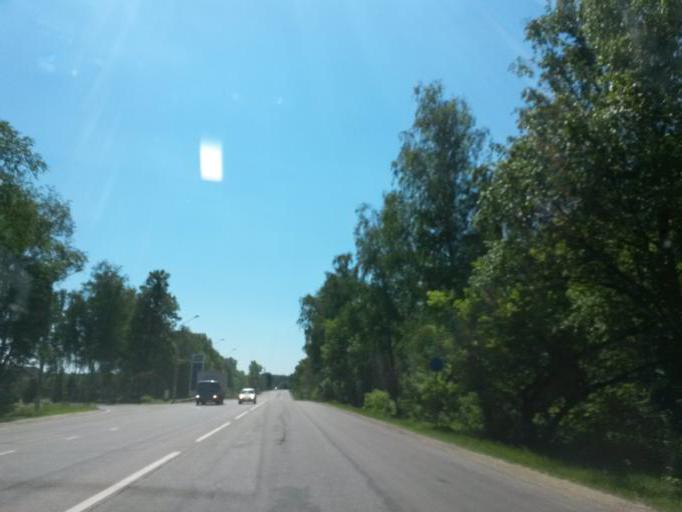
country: RU
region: Moskovskaya
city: Stolbovaya
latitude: 55.2103
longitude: 37.5065
